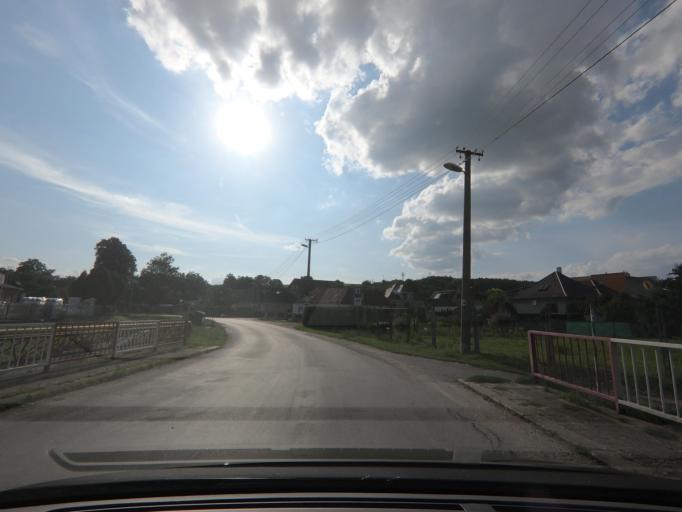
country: SK
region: Nitriansky
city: Stara Tura
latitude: 48.7381
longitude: 17.7219
